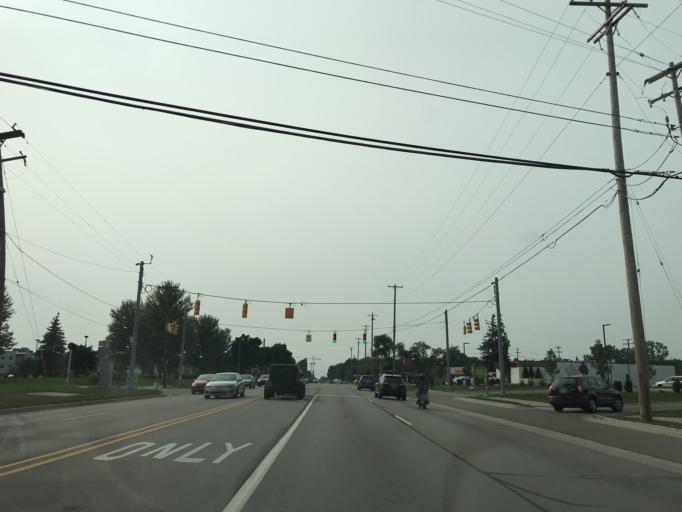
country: US
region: Michigan
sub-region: Ingham County
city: Okemos
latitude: 42.7267
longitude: -84.4523
